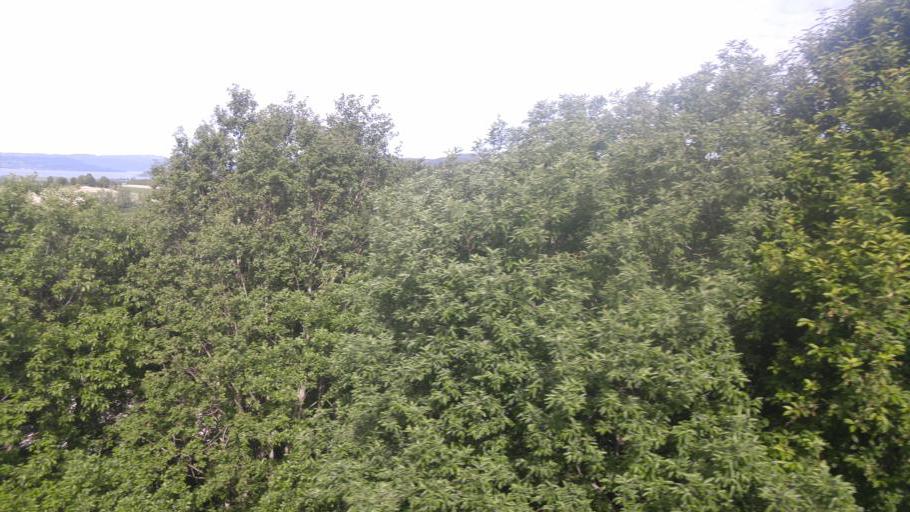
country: NO
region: Sor-Trondelag
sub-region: Melhus
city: Melhus
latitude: 63.3336
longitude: 10.3427
